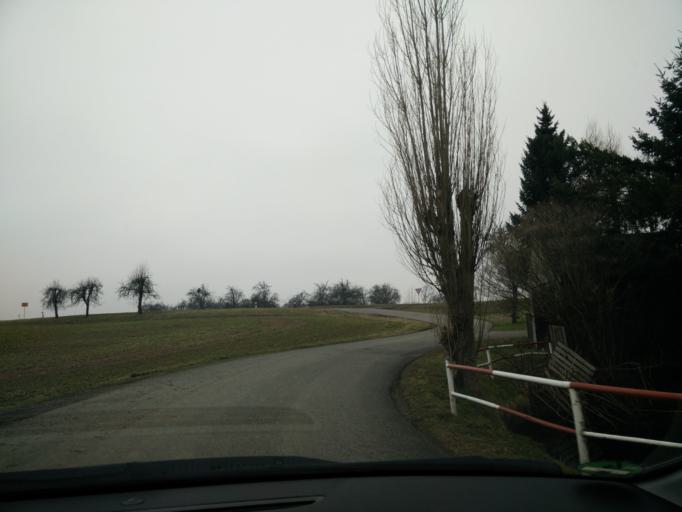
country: DE
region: Saxony
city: Wechselburg
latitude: 50.9845
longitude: 12.7579
